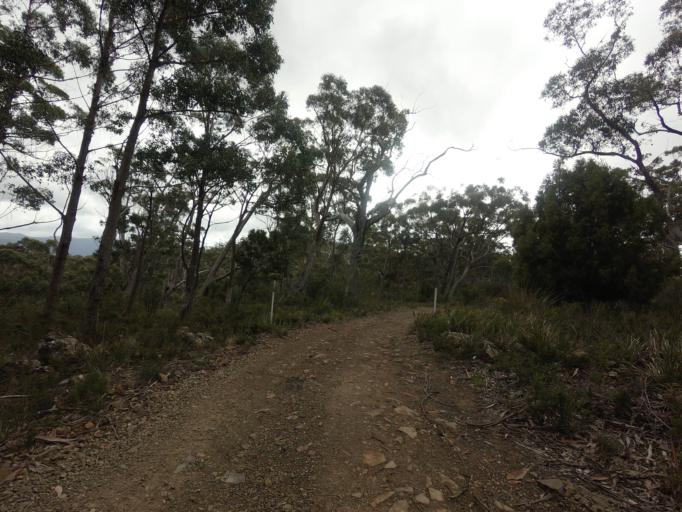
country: AU
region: Tasmania
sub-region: Huon Valley
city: Geeveston
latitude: -43.4605
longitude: 146.9092
